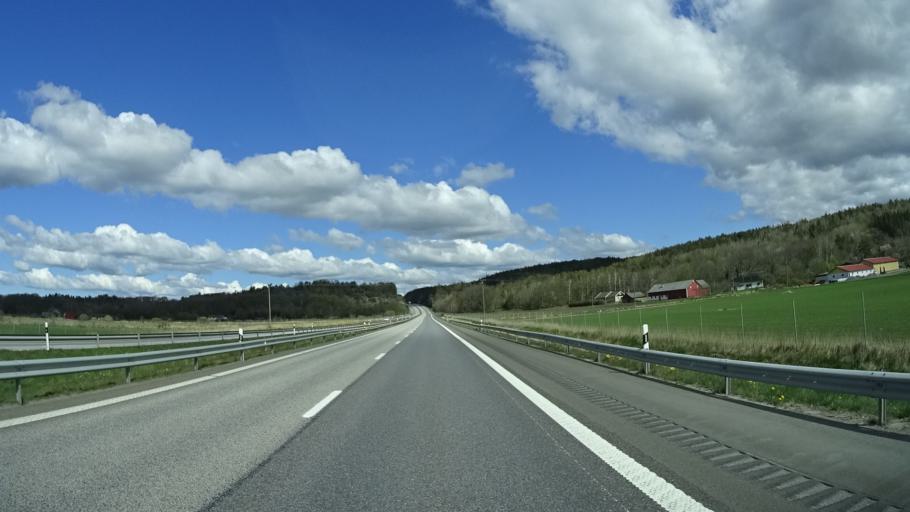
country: SE
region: Halland
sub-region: Kungsbacka Kommun
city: Frillesas
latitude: 57.2994
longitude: 12.2155
